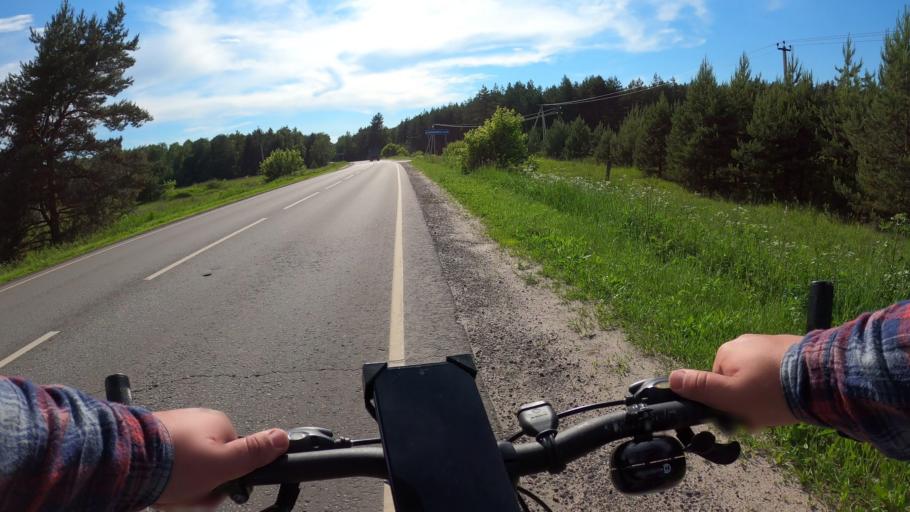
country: RU
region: Moskovskaya
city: Konobeyevo
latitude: 55.4356
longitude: 38.6356
